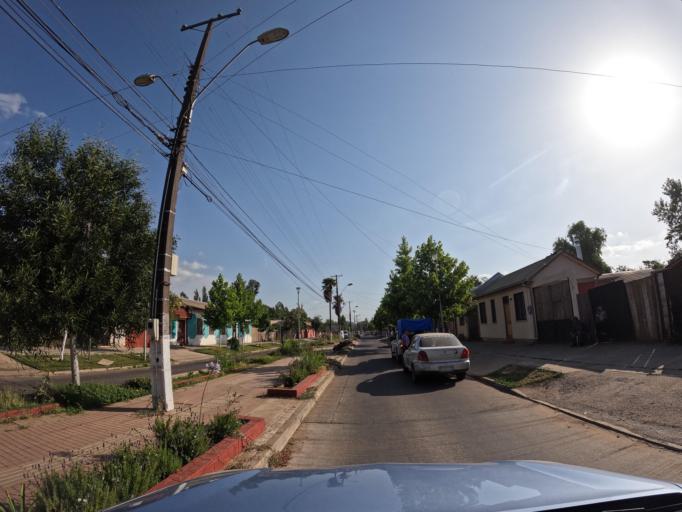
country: CL
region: Maule
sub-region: Provincia de Curico
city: Molina
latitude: -35.2849
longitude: -71.2611
